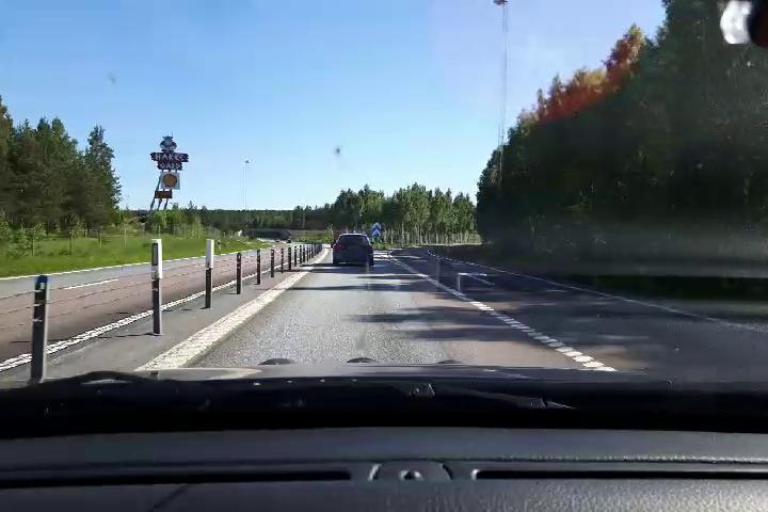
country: SE
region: Gaevleborg
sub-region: Gavle Kommun
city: Norrsundet
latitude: 60.9053
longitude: 17.0153
